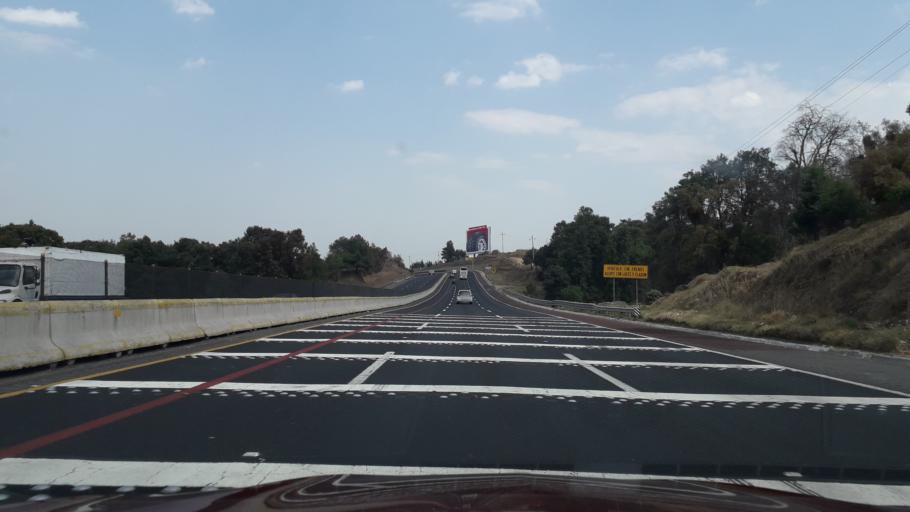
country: MX
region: Puebla
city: Santa Rita Tlahuapan
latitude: 19.3446
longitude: -98.5967
